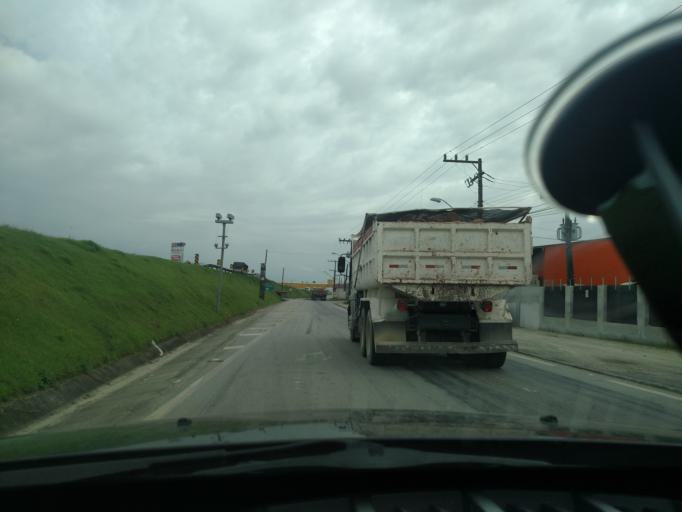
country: BR
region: Santa Catarina
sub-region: Itajai
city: Itajai
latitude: -26.8718
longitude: -48.7288
